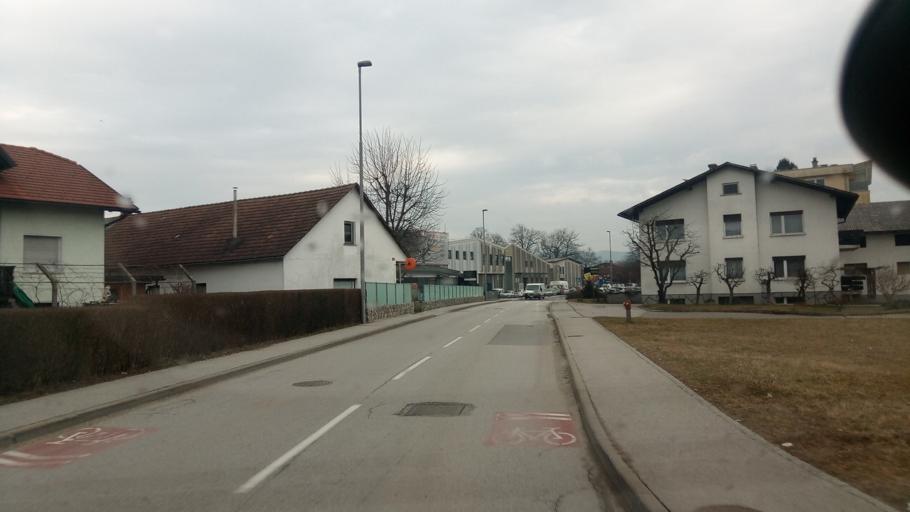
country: SI
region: Menges
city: Preserje pri Radomljah
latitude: 46.1679
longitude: 14.5961
